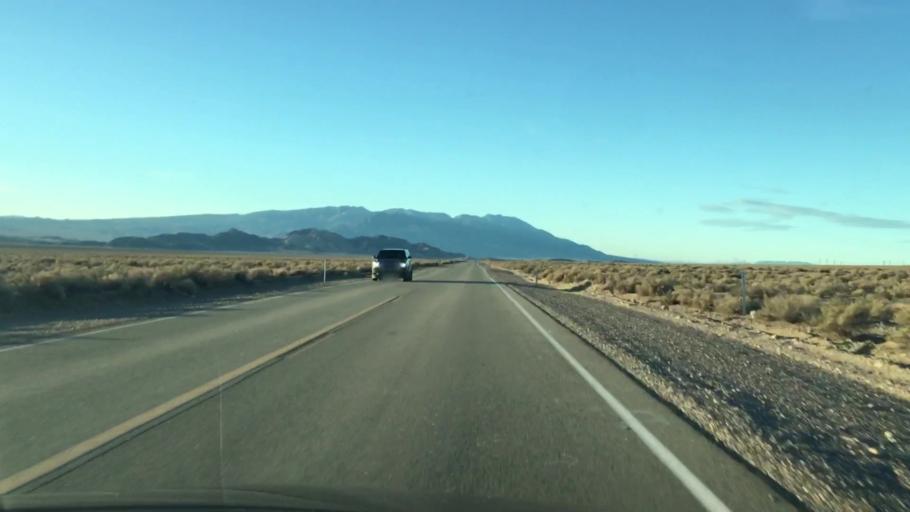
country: US
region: California
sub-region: San Bernardino County
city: Fort Irwin
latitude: 35.3486
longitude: -116.0880
